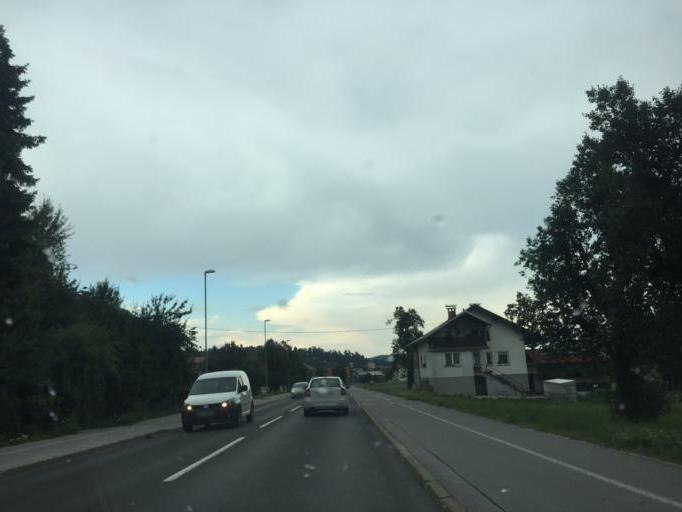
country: SI
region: Logatec
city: Logatec
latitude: 45.9131
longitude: 14.2078
